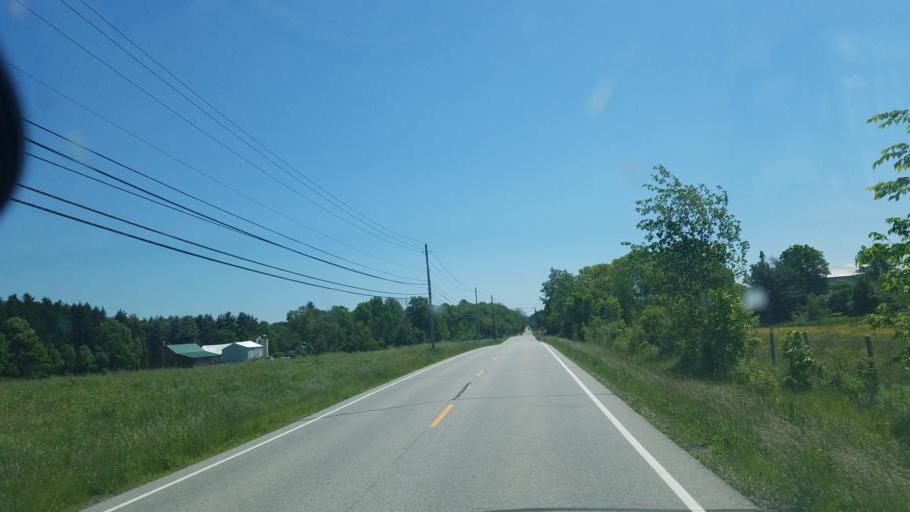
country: US
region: Ohio
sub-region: Geauga County
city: Bainbridge
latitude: 41.4328
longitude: -81.2761
